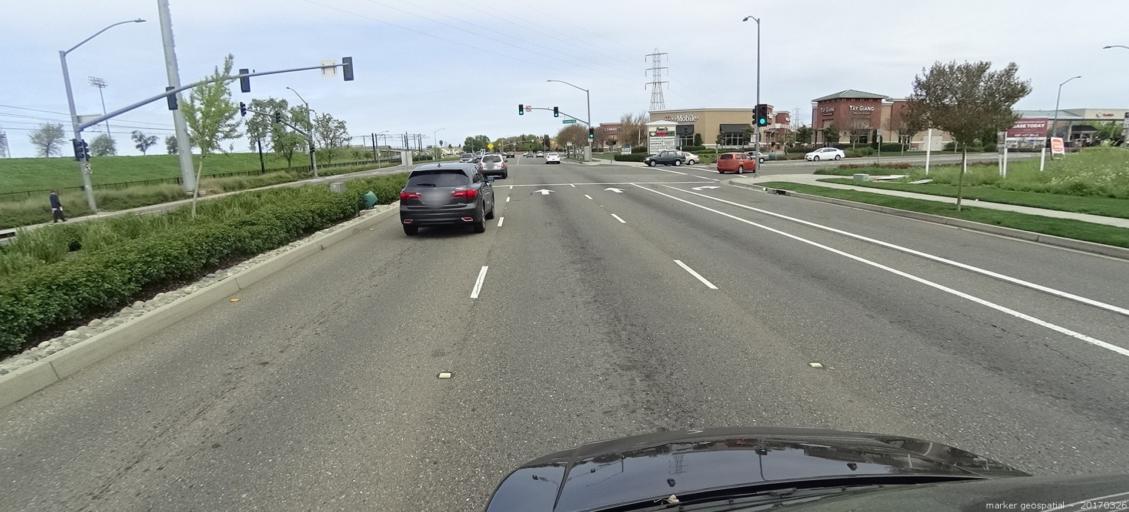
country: US
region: California
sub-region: Sacramento County
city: Laguna
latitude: 38.4547
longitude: -121.4178
